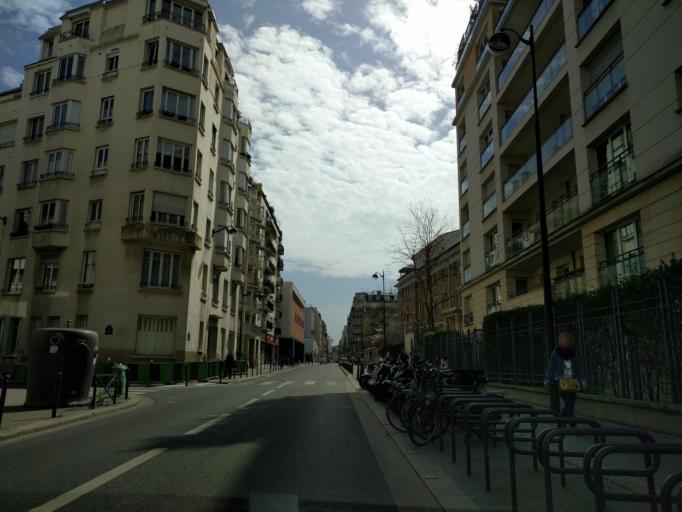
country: FR
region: Ile-de-France
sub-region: Departement du Val-de-Marne
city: Saint-Mande
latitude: 48.8425
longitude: 2.3976
